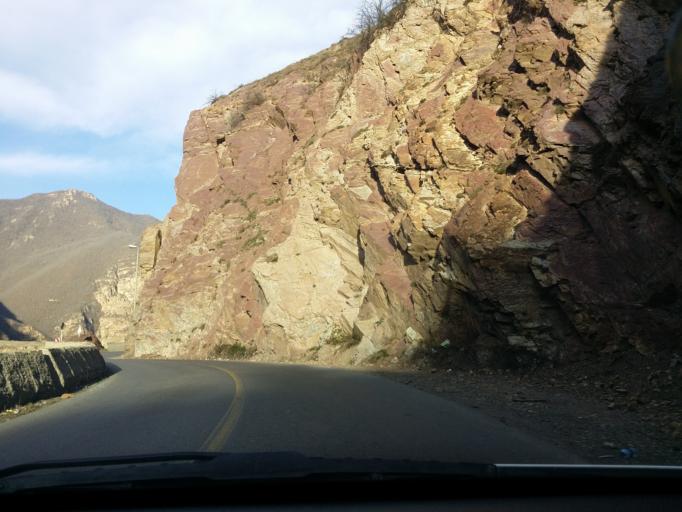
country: IR
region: Mazandaran
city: Chalus
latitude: 36.2642
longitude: 51.2637
